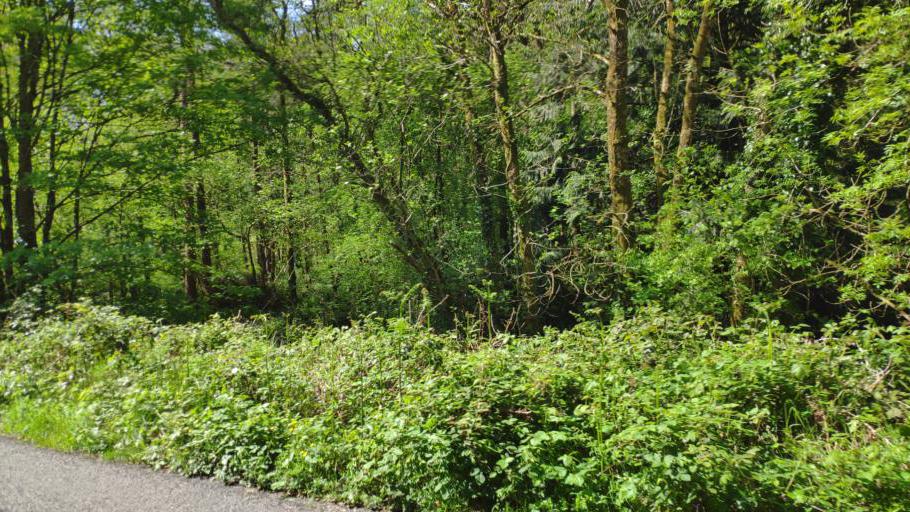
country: IE
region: Munster
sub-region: County Cork
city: Blarney
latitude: 51.9783
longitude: -8.5840
